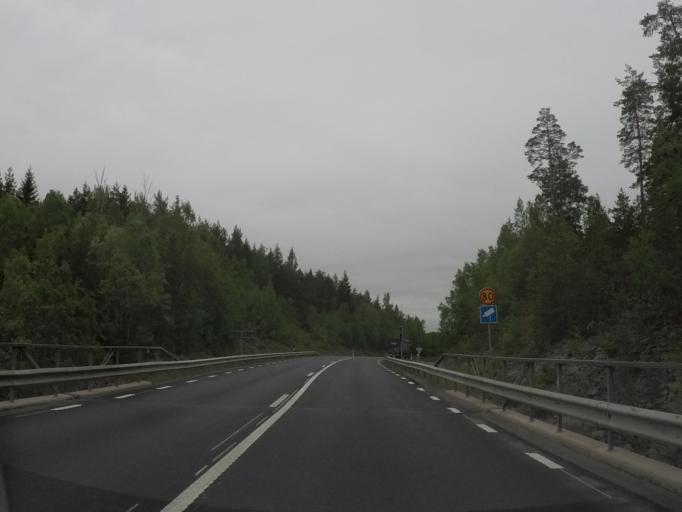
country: SE
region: Soedermanland
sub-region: Flens Kommun
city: Flen
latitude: 59.0627
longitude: 16.6212
